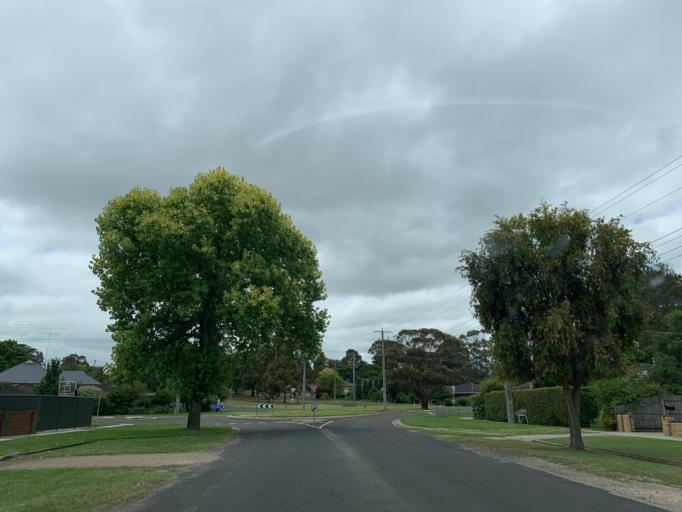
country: AU
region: Victoria
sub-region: Wellington
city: Sale
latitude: -37.9614
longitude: 146.9761
